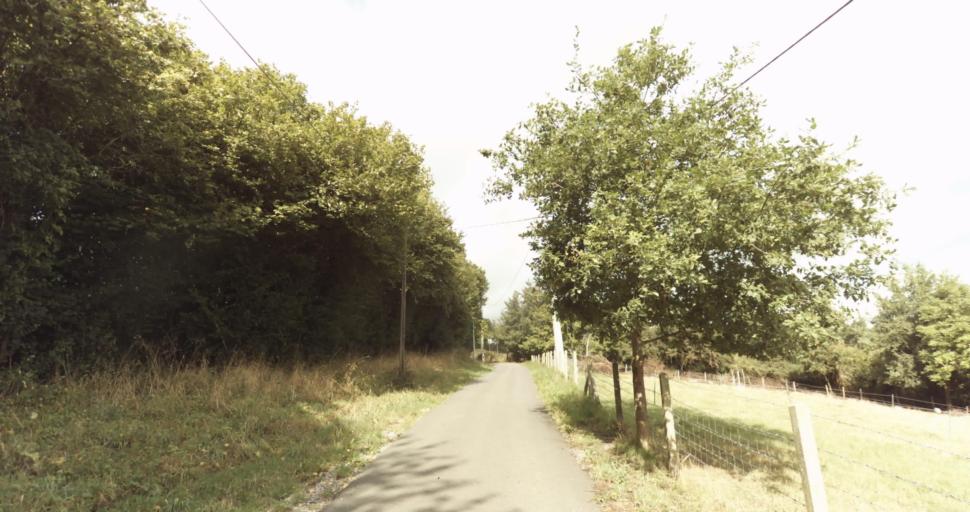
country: FR
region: Lower Normandy
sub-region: Departement de l'Orne
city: Gace
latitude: 48.8084
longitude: 0.2732
